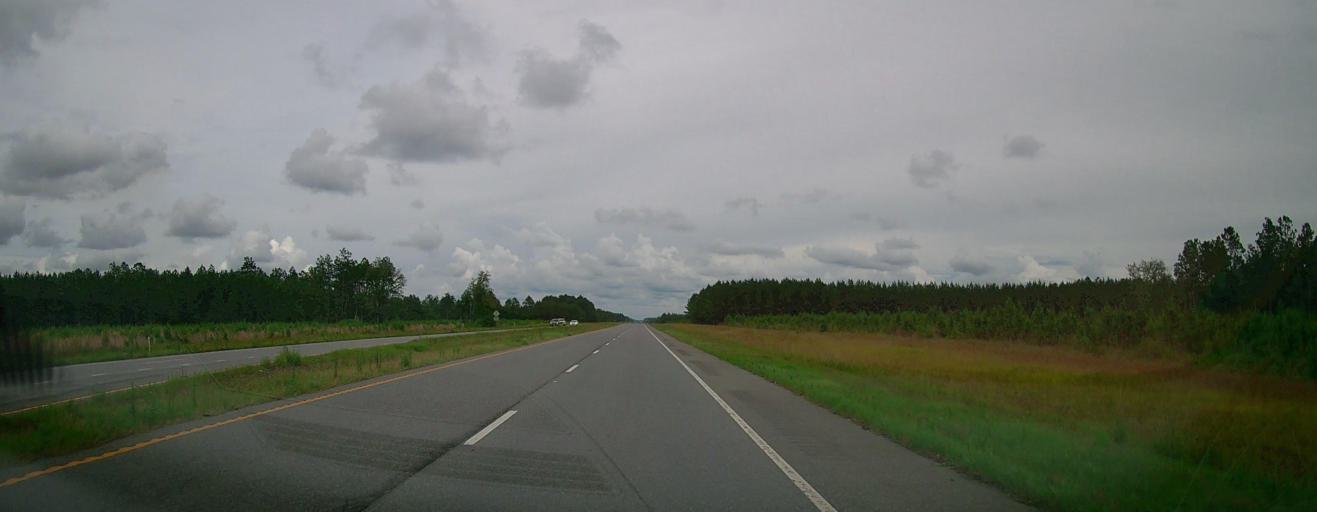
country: US
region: Georgia
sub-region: Appling County
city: Baxley
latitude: 31.7554
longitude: -82.2821
